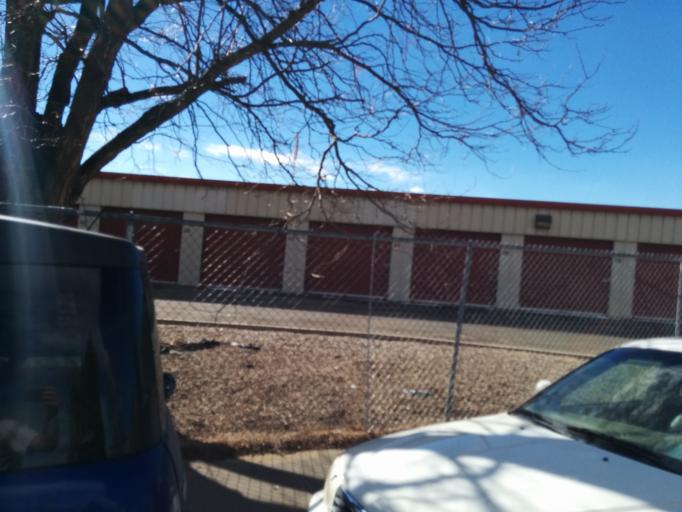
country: US
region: Colorado
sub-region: Larimer County
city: Fort Collins
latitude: 40.5620
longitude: -105.0787
